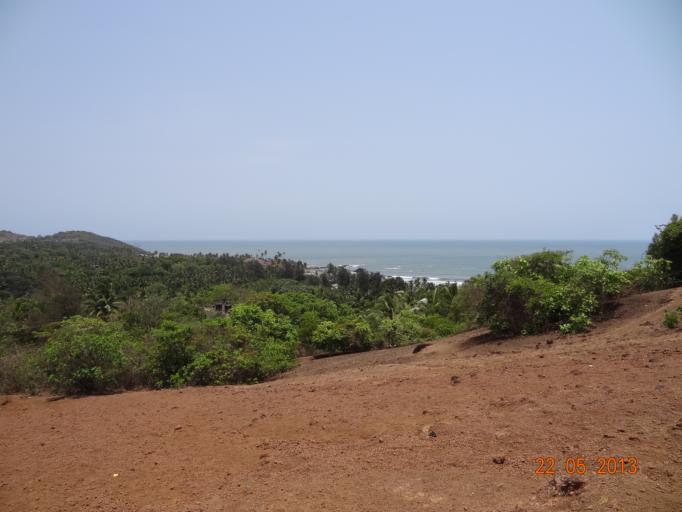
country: IN
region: Goa
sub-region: North Goa
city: Vagator
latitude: 15.6045
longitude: 73.7369
